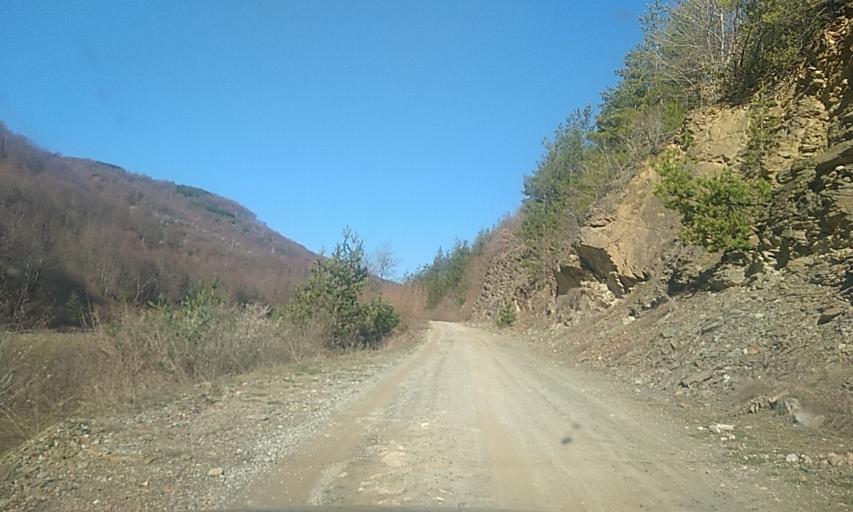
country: MK
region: Kriva Palanka
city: Kriva Palanka
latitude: 42.3406
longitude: 22.3897
